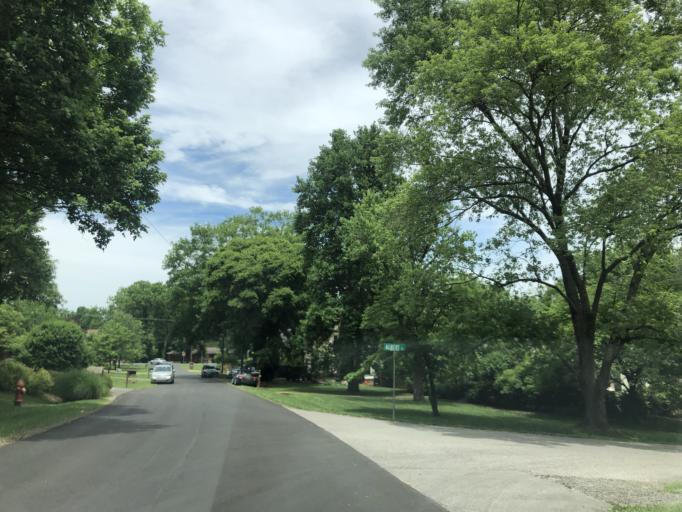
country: US
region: Tennessee
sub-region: Davidson County
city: Oak Hill
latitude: 36.1044
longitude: -86.7877
